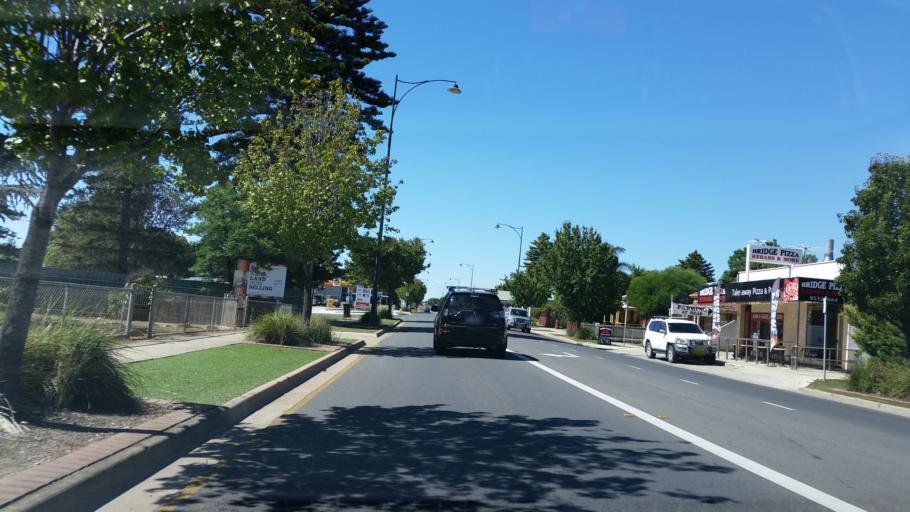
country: AU
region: South Australia
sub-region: Murray Bridge
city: Murray Bridge
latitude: -35.1225
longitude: 139.2676
